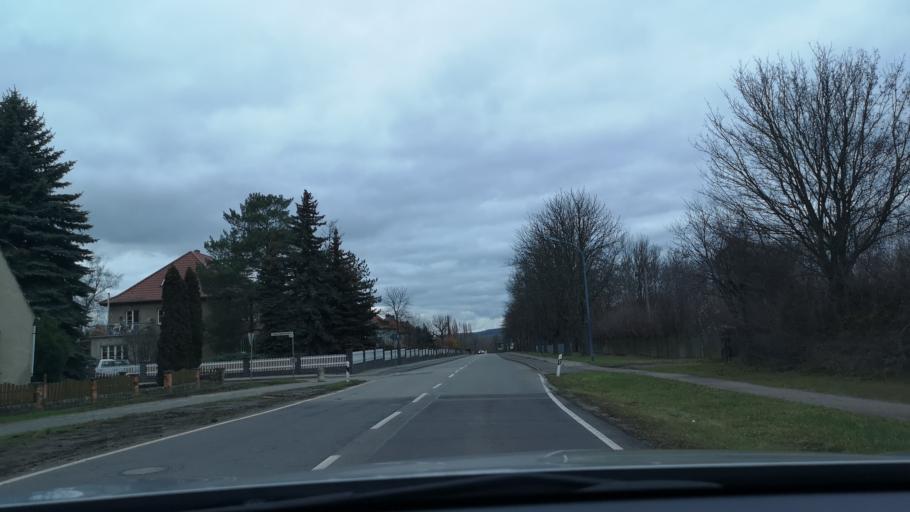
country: DE
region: Saxony-Anhalt
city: Krumpa
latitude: 51.2917
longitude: 11.8547
